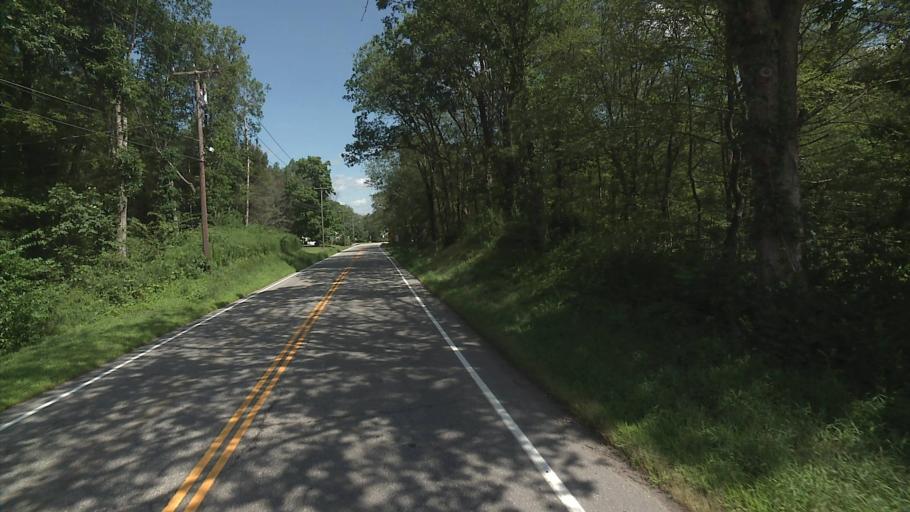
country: US
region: Connecticut
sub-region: Windham County
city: South Woodstock
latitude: 41.8746
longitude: -72.0876
